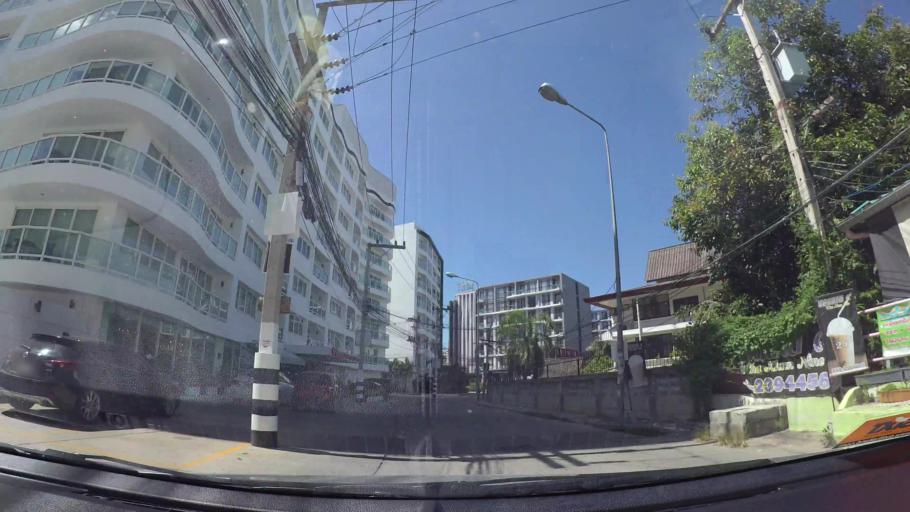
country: TH
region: Chon Buri
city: Phatthaya
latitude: 12.9393
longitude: 100.8902
